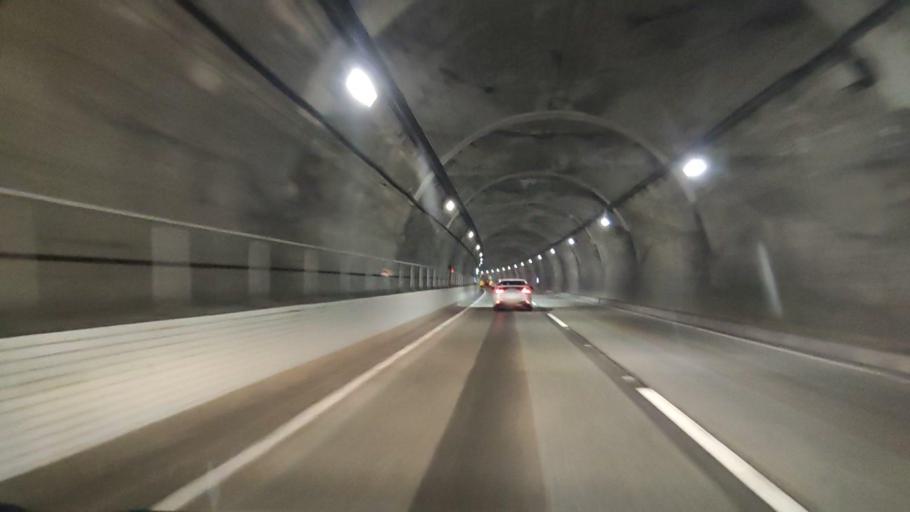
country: JP
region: Iwate
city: Ichinohe
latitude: 40.2339
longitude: 141.3912
